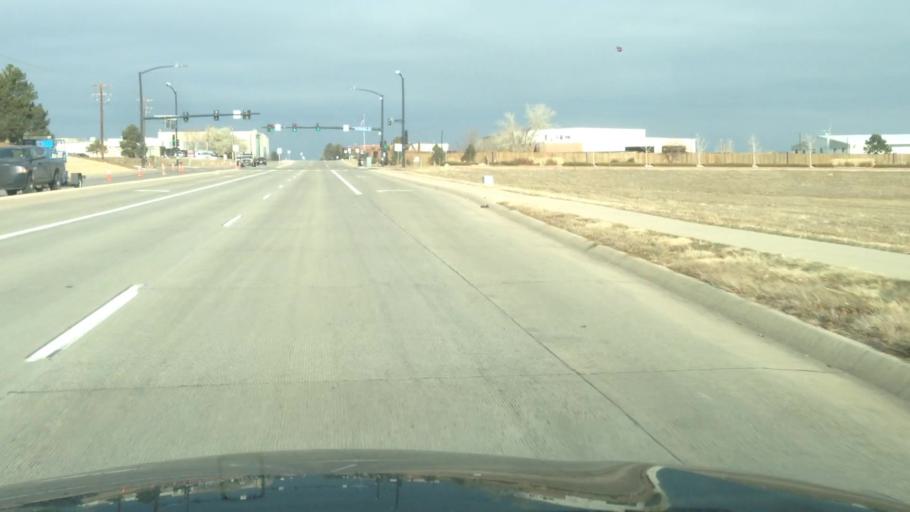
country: US
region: Colorado
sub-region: Arapahoe County
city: Dove Valley
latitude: 39.5854
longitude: -104.8155
